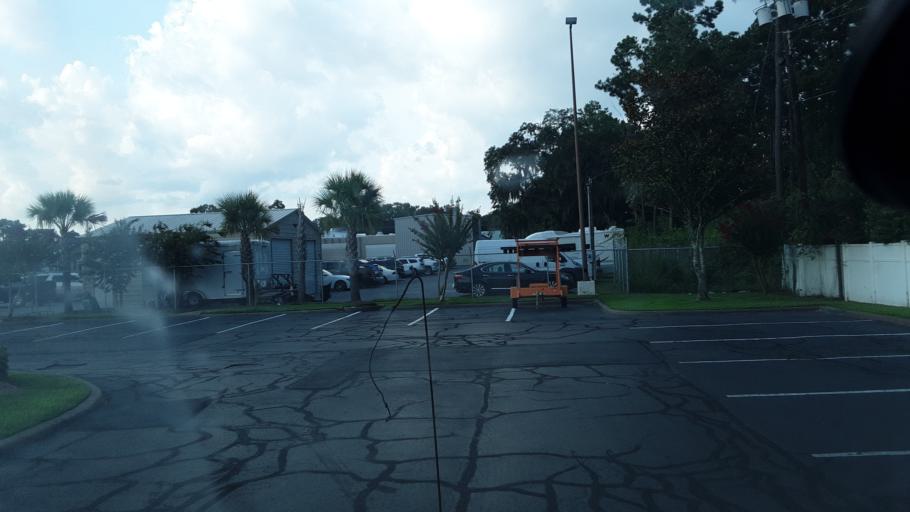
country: US
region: Georgia
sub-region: Chatham County
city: Isle of Hope
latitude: 32.0113
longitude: -81.1122
